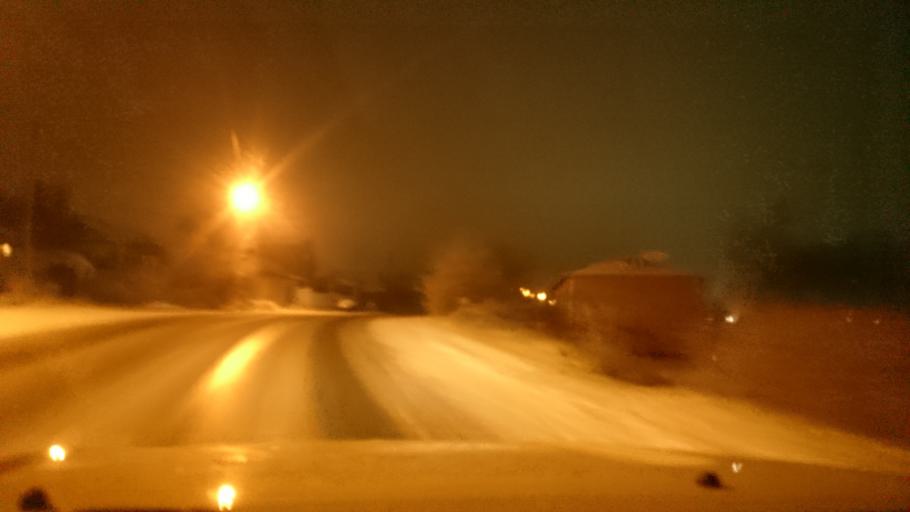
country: RU
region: Tula
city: Gorelki
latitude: 54.2357
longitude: 37.5513
